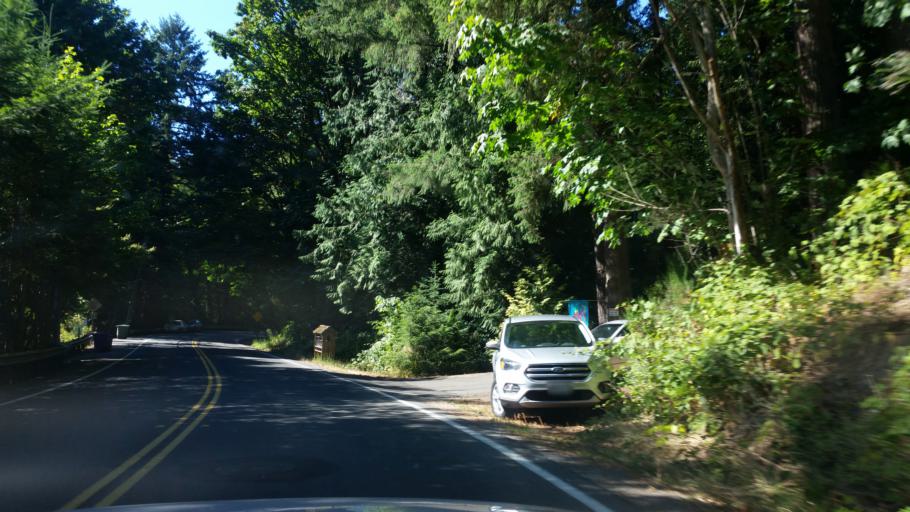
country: US
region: Washington
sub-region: King County
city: Lake Forest Park
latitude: 47.7683
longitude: -122.2842
